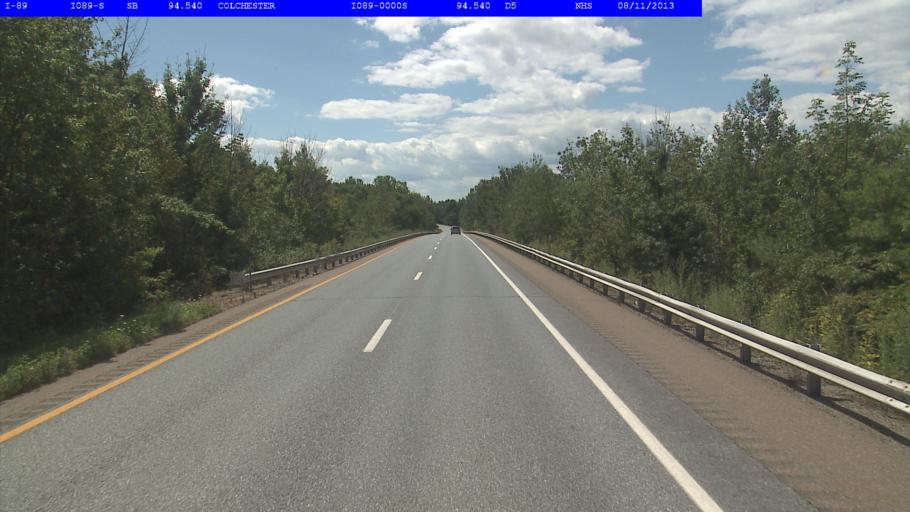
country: US
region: Vermont
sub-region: Chittenden County
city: Colchester
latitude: 44.5452
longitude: -73.1942
